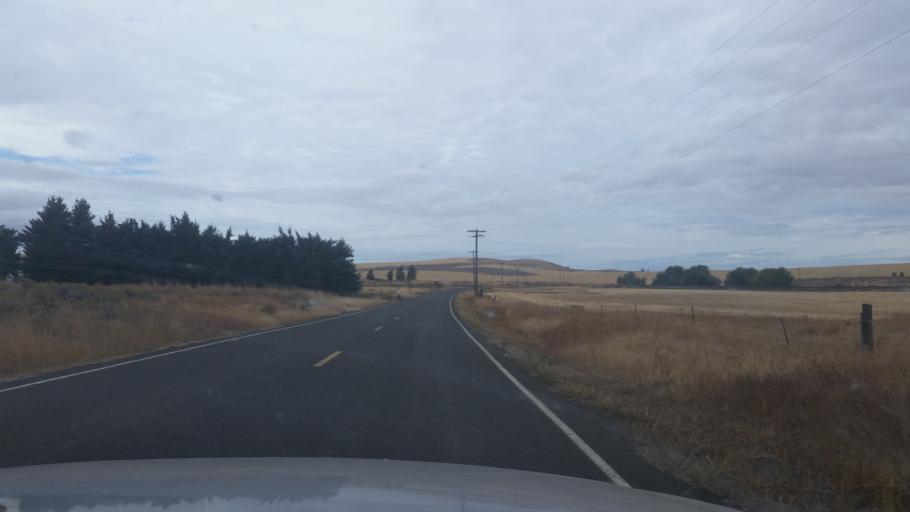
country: US
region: Washington
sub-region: Spokane County
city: Medical Lake
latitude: 47.5178
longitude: -117.8960
